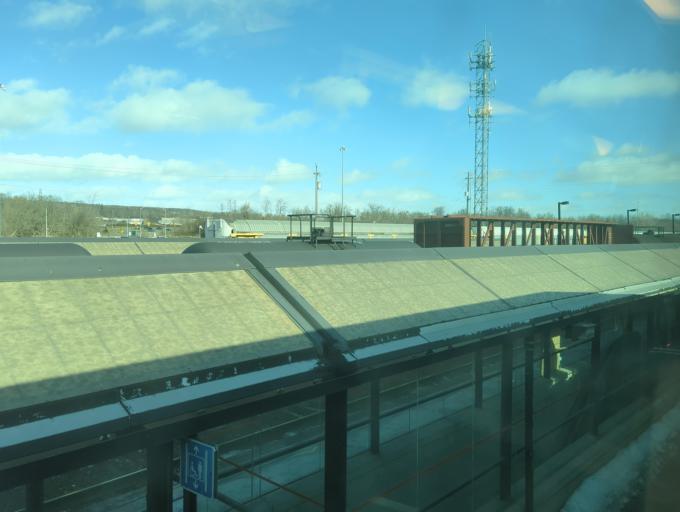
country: CA
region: Ontario
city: Hamilton
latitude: 43.3129
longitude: -79.8552
